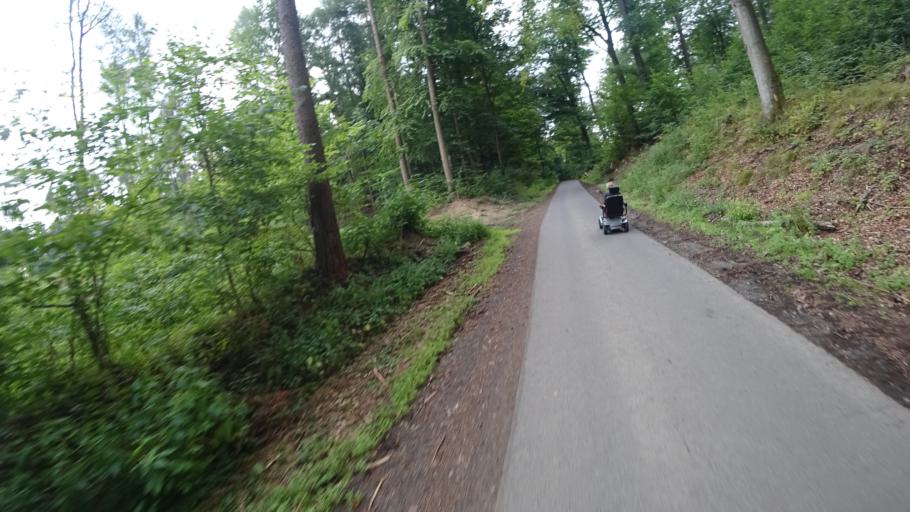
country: DE
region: Rheinland-Pfalz
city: Hohr-Grenzhausen
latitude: 50.4248
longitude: 7.6617
